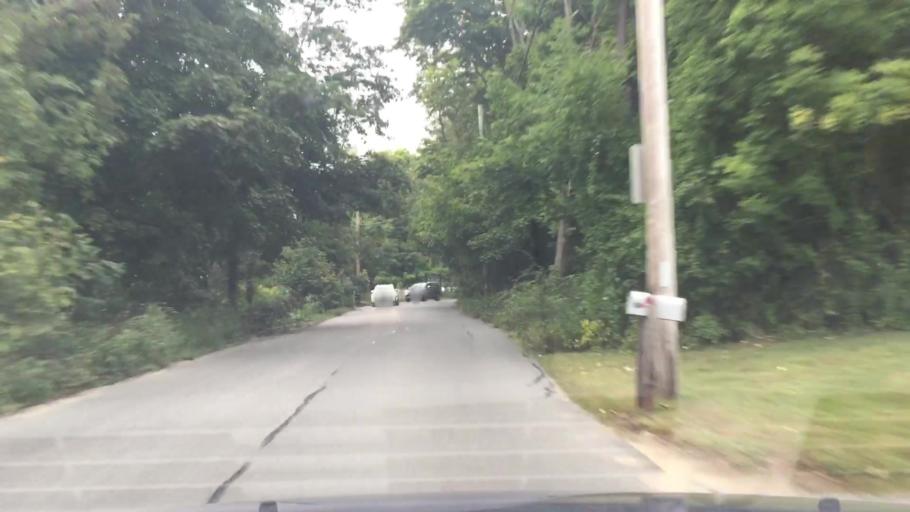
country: US
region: Massachusetts
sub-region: Essex County
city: North Andover
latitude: 42.6995
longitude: -71.0773
